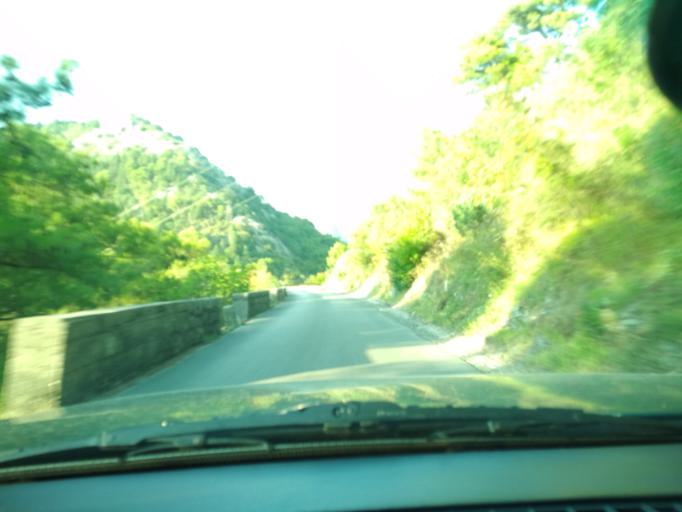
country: ME
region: Kotor
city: Kotor
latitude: 42.4008
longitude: 18.7600
